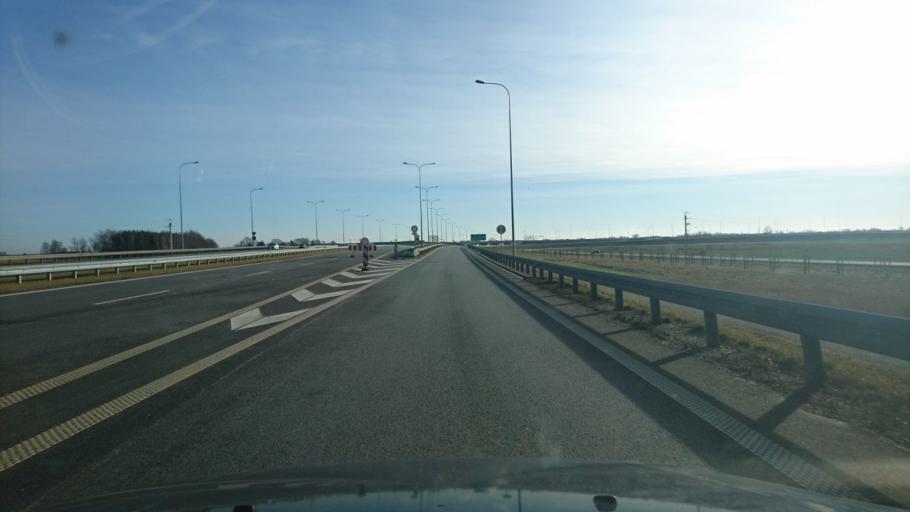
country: PL
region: Greater Poland Voivodeship
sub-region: Powiat kepinski
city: Kepno
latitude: 51.3210
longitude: 18.0030
